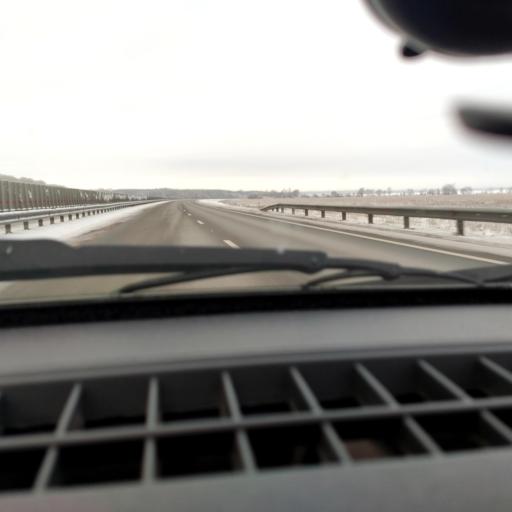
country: RU
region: Bashkortostan
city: Kushnarenkovo
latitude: 55.0614
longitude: 55.3911
